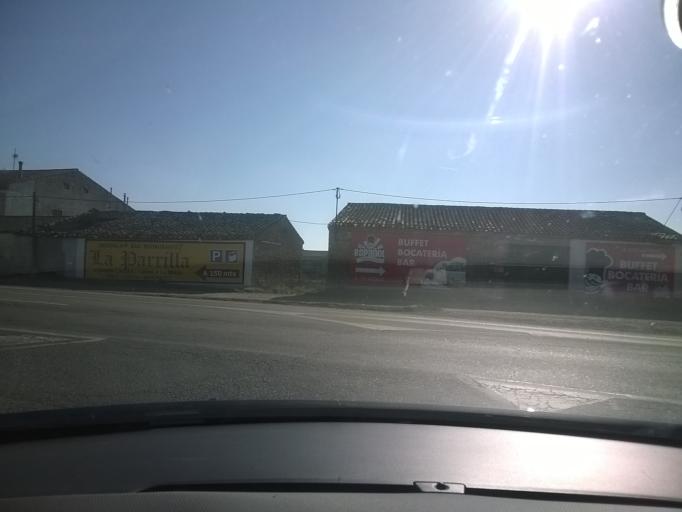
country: ES
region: Aragon
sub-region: Provincia de Zaragoza
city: Bujaraloz
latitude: 41.4967
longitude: -0.1558
